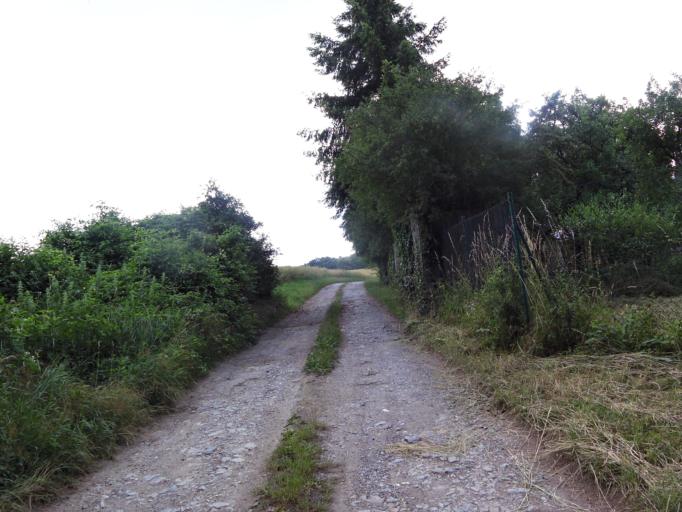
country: DE
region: Bavaria
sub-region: Regierungsbezirk Unterfranken
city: Wuerzburg
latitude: 49.8119
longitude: 9.9280
